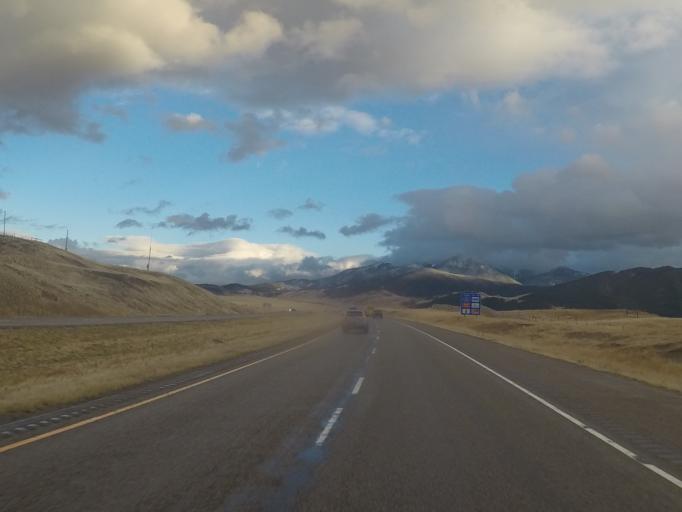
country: US
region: Montana
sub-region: Park County
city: Livingston
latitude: 45.6484
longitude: -110.6035
